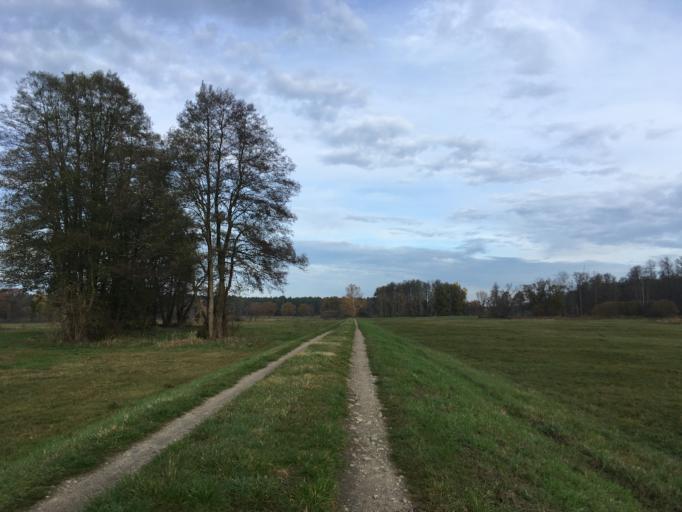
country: DE
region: Brandenburg
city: Schlepzig
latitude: 52.0295
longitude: 13.8544
